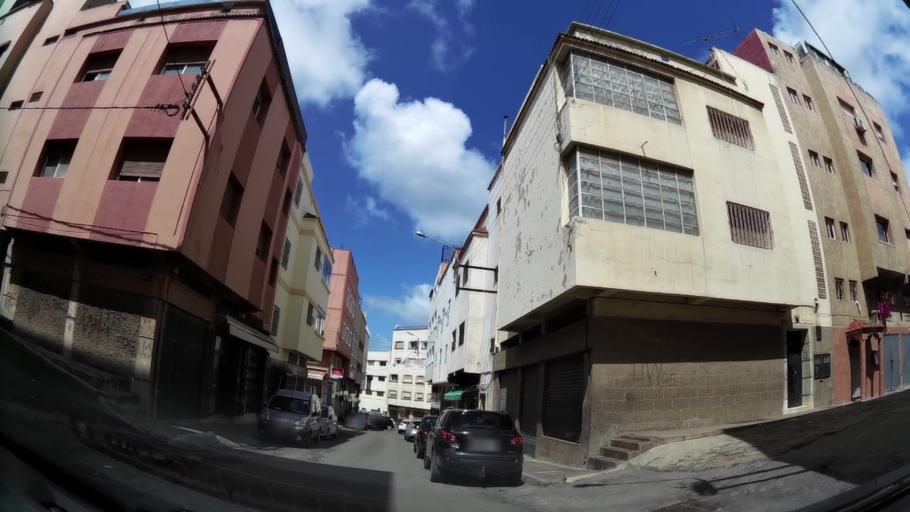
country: MA
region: Grand Casablanca
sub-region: Casablanca
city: Casablanca
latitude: 33.5404
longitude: -7.5928
